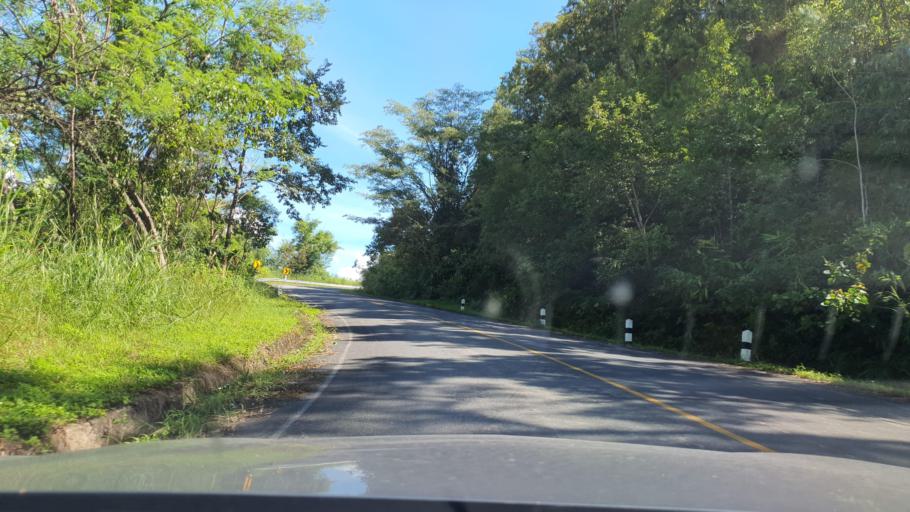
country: TH
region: Chiang Mai
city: Phrao
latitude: 19.3549
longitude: 99.2751
